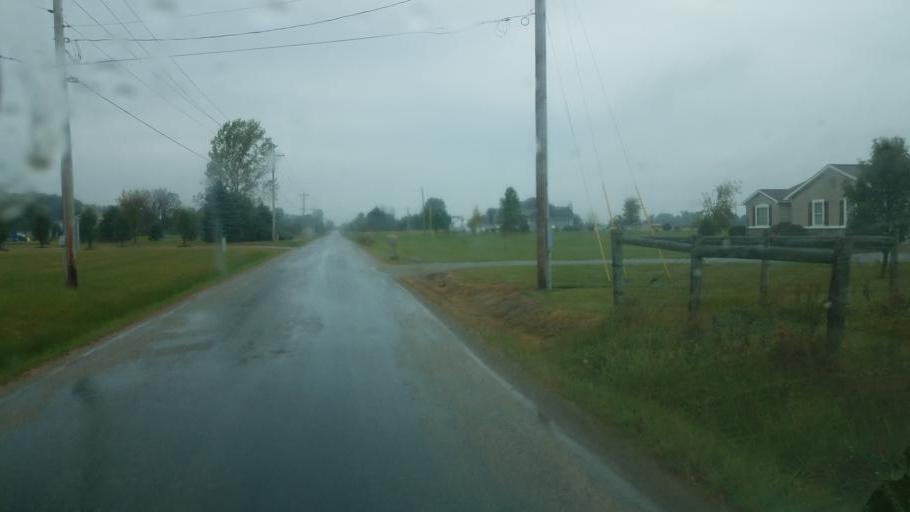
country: US
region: Ohio
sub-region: Ashland County
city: Ashland
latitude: 40.8145
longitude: -82.3413
